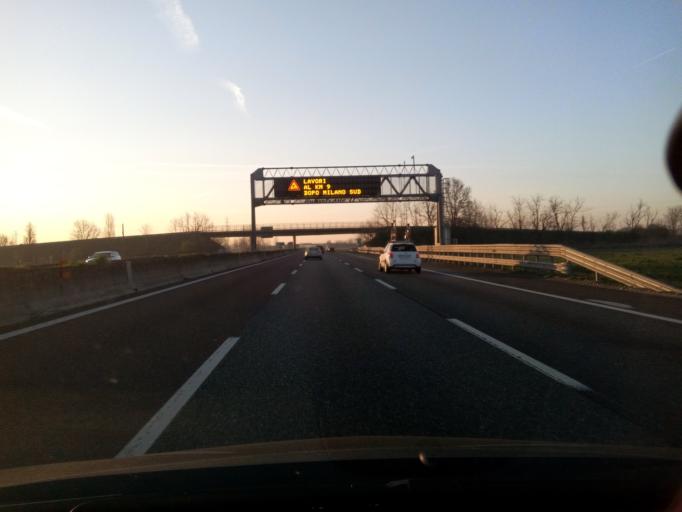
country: IT
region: Lombardy
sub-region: Citta metropolitana di Milano
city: San Giuliano Milanese
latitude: 45.3703
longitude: 9.2852
